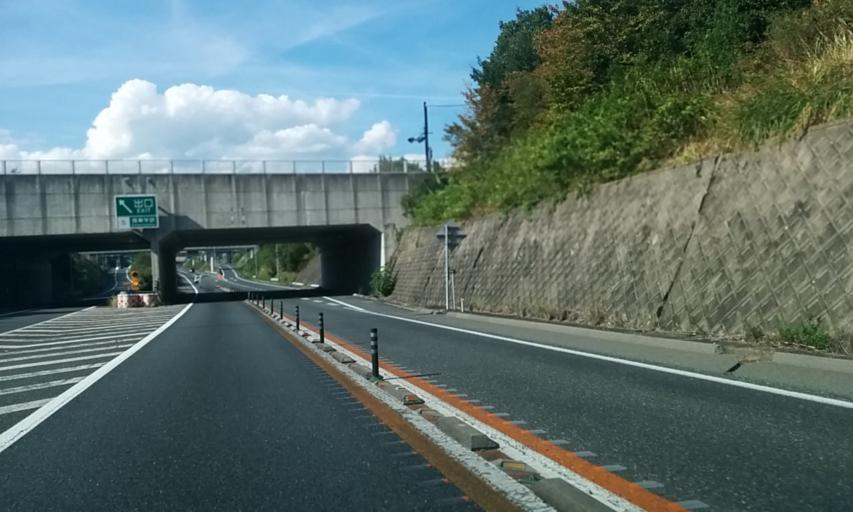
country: JP
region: Nara
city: Nara-shi
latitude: 34.7431
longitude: 135.7874
